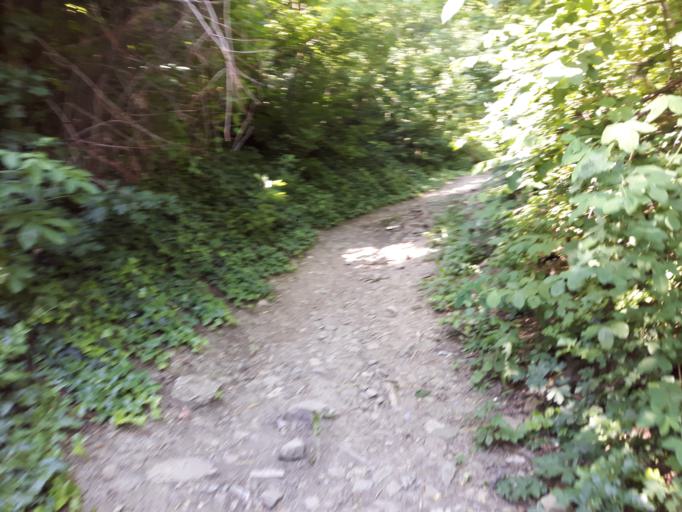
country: AT
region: Lower Austria
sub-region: Politischer Bezirk Wien-Umgebung
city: Klosterneuburg
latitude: 48.2570
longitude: 16.2939
